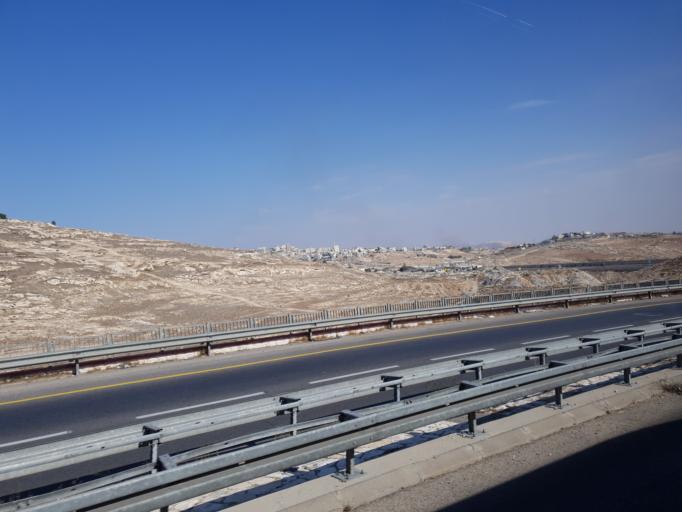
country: PS
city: Az Za`ayyim
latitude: 31.7906
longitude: 35.2531
